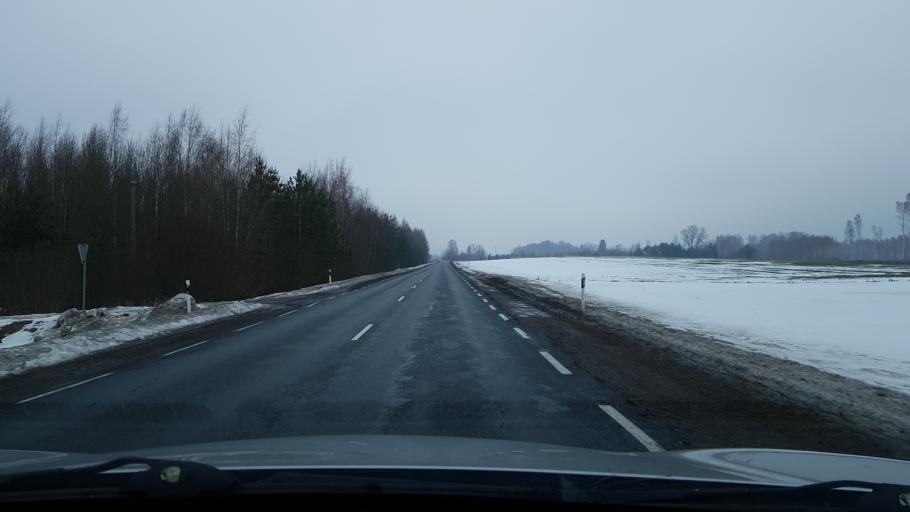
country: EE
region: Valgamaa
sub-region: Torva linn
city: Torva
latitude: 58.1300
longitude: 25.9919
